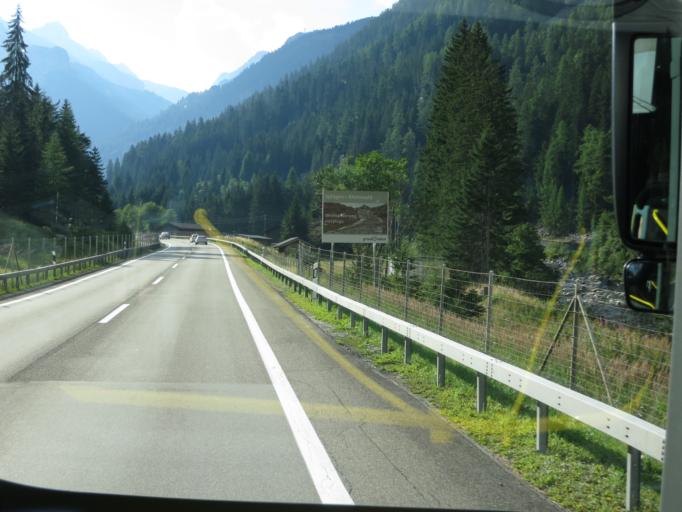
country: CH
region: Grisons
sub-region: Hinterrhein District
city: Thusis
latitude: 46.5672
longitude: 9.3934
